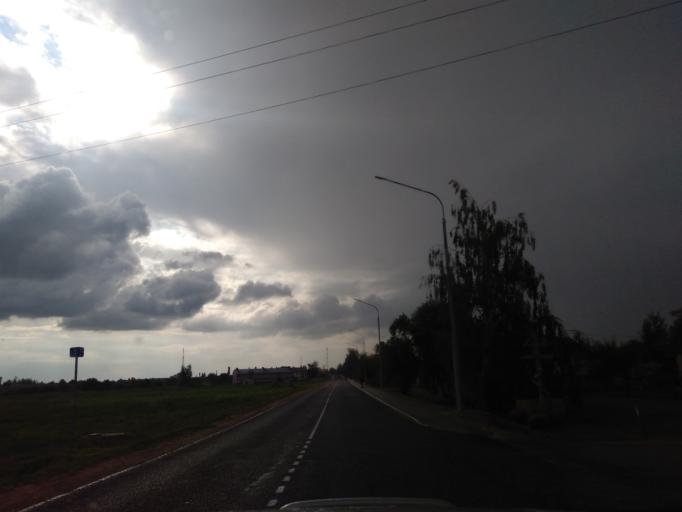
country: BY
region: Minsk
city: Kapyl'
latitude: 53.1420
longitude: 27.1128
